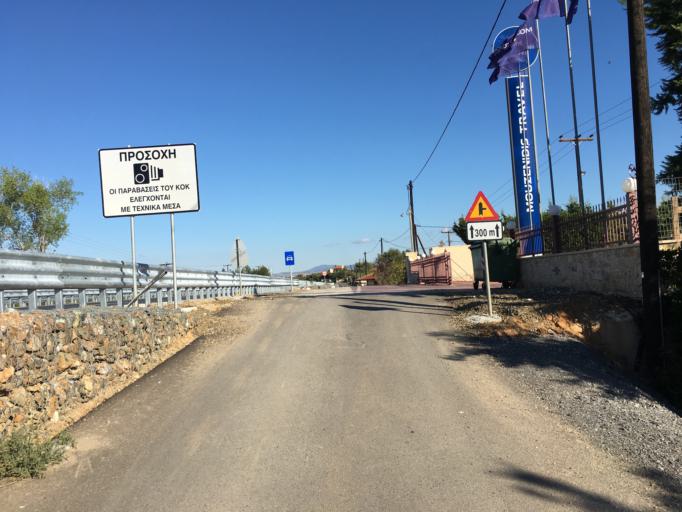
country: GR
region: Central Macedonia
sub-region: Nomos Chalkidikis
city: Nea Potidhaia
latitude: 40.2144
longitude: 23.3214
